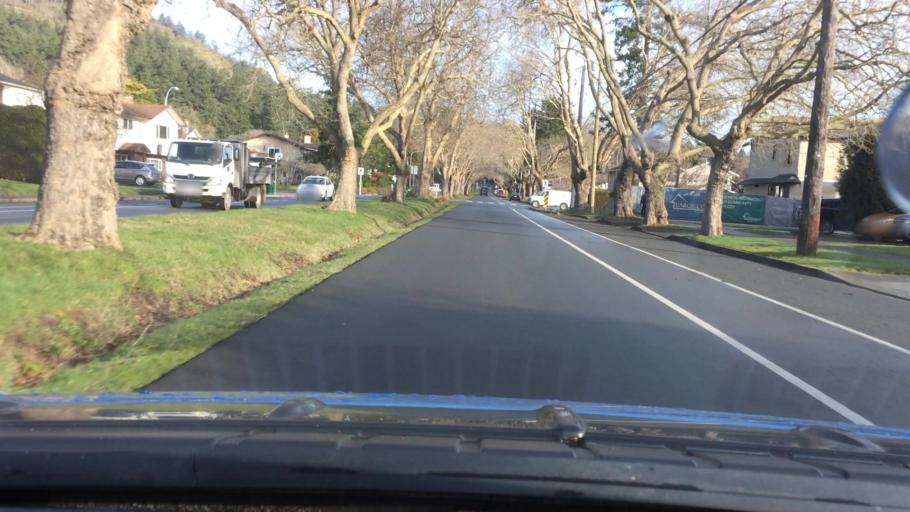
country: CA
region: British Columbia
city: Oak Bay
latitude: 48.4859
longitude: -123.3372
